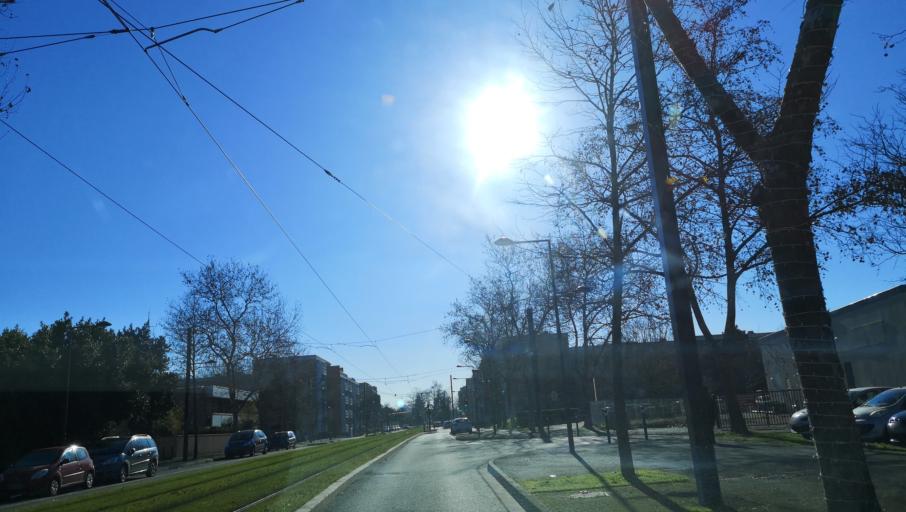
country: FR
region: Midi-Pyrenees
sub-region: Departement de la Haute-Garonne
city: Blagnac
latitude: 43.6386
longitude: 1.3832
